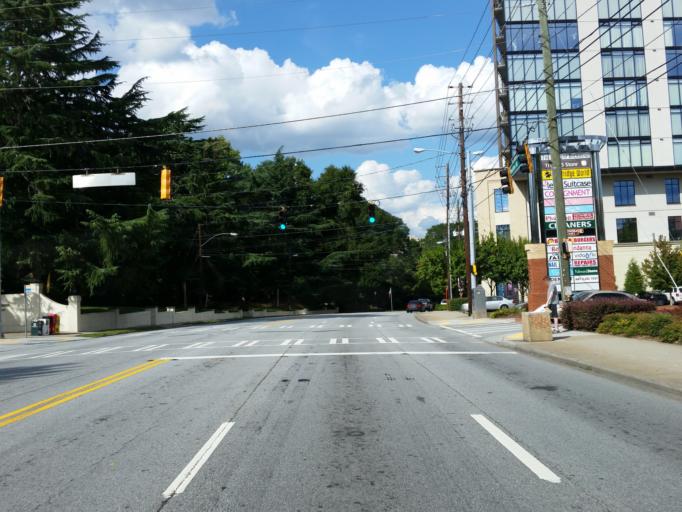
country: US
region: Georgia
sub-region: DeKalb County
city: Druid Hills
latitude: 33.8145
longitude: -84.3919
